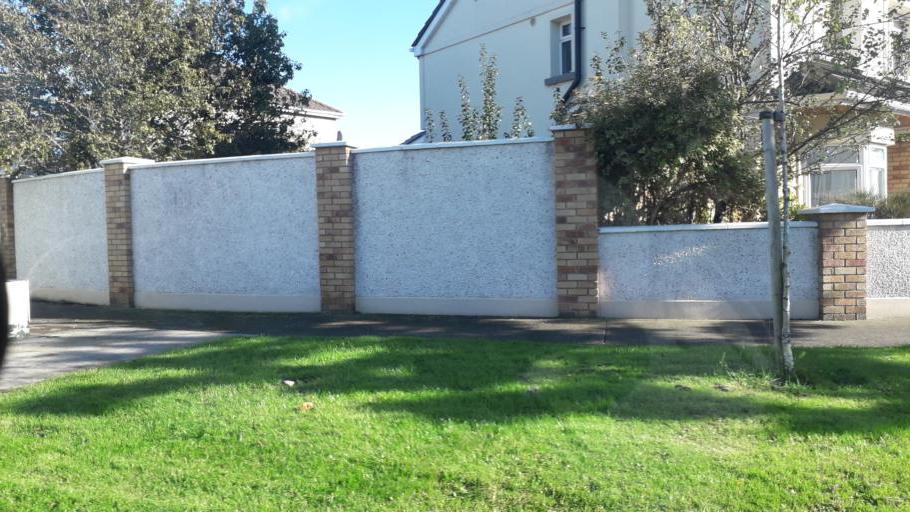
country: IE
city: Coolock
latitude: 53.3874
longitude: -6.1936
